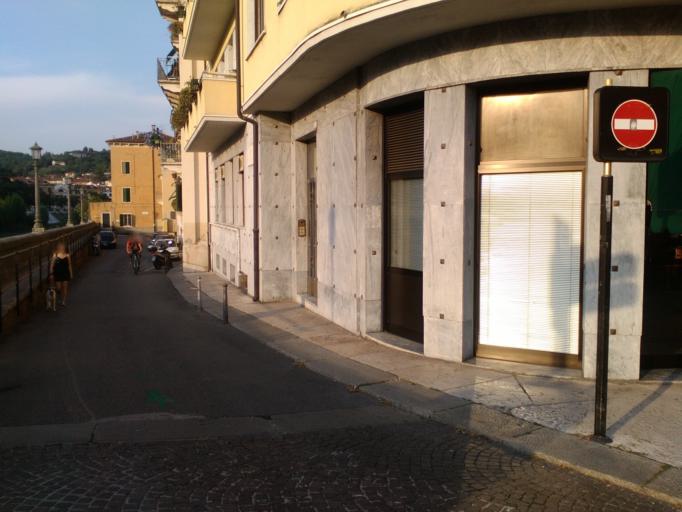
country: IT
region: Veneto
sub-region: Provincia di Verona
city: Verona
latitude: 45.4466
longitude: 10.9947
